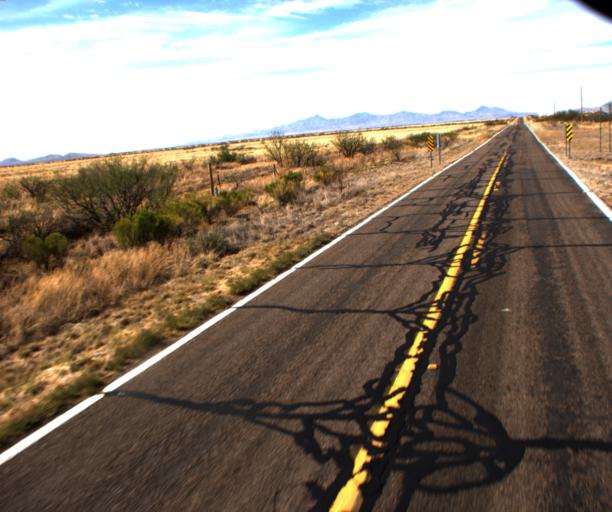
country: US
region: Arizona
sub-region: Cochise County
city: Willcox
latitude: 31.9138
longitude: -109.4914
